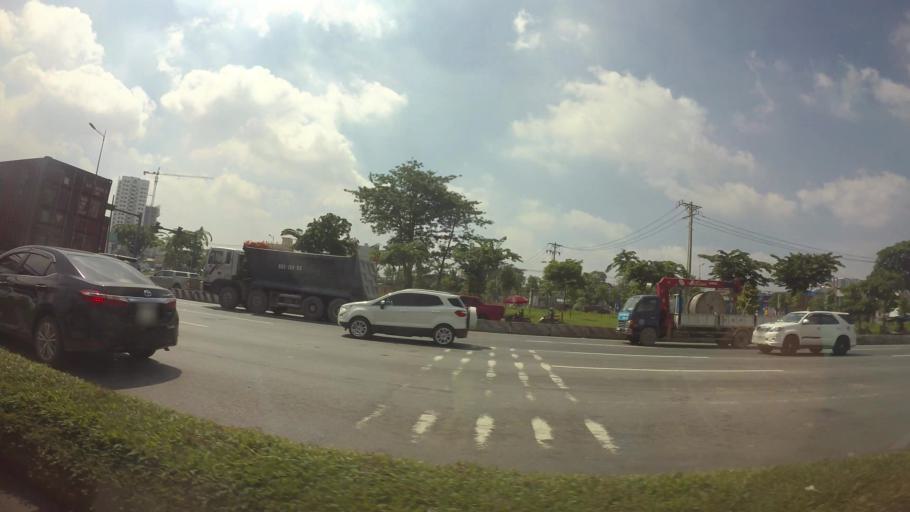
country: VN
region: Ho Chi Minh City
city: Quan Chin
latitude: 10.8237
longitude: 106.7593
